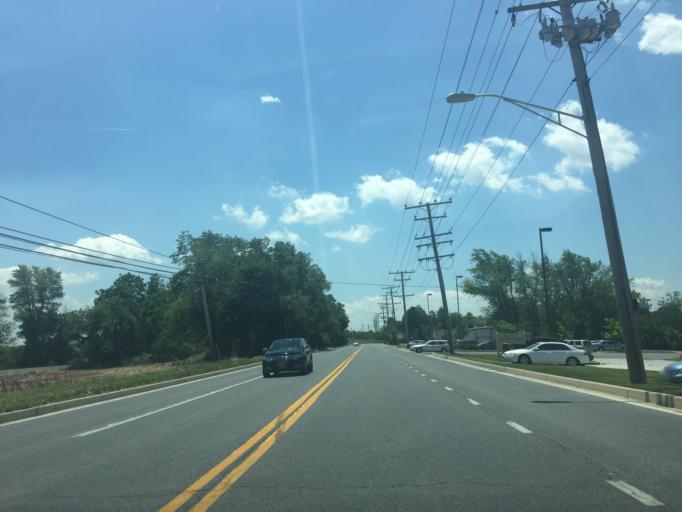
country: US
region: Maryland
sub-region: Carroll County
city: Hampstead
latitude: 39.5852
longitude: -76.8424
